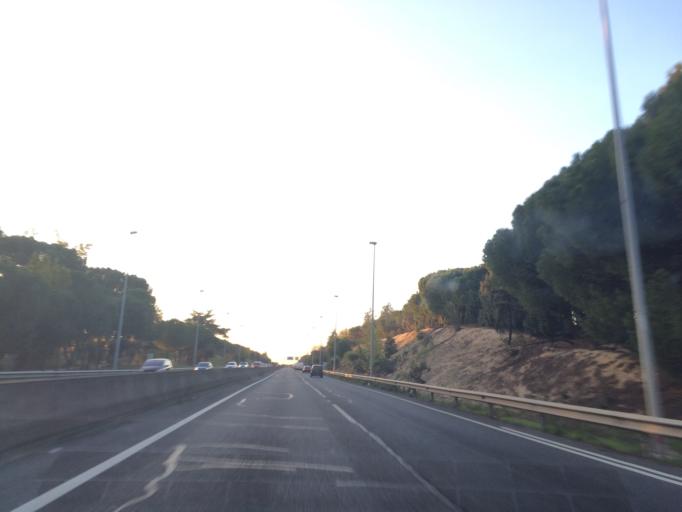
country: ES
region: Madrid
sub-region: Provincia de Madrid
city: Moncloa-Aravaca
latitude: 40.4453
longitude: -3.7538
